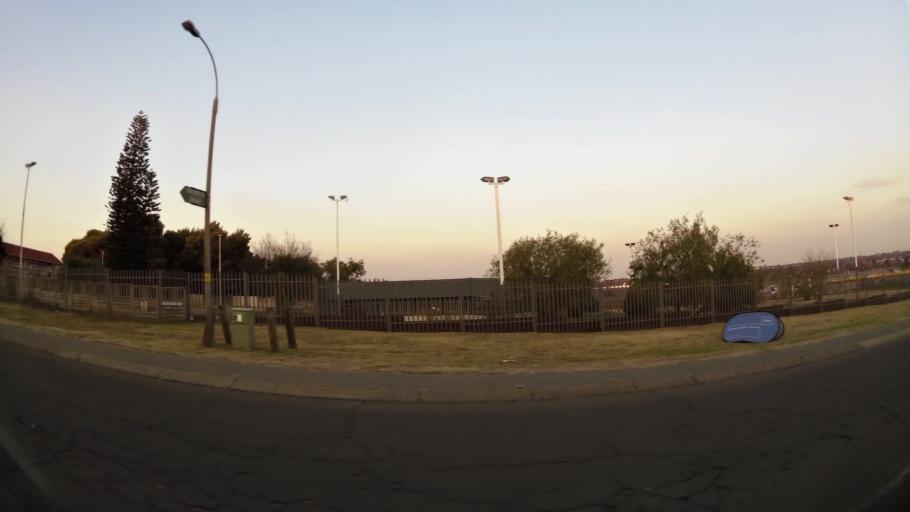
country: ZA
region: Gauteng
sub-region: City of Johannesburg Metropolitan Municipality
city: Modderfontein
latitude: -26.0673
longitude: 28.2292
